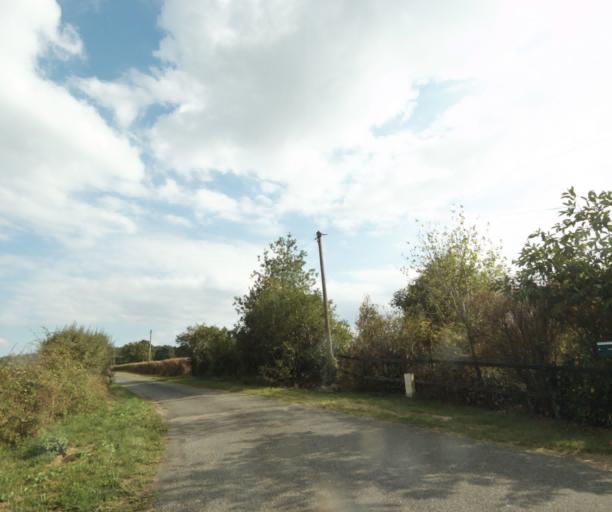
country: FR
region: Bourgogne
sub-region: Departement de Saone-et-Loire
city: Palinges
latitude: 46.5108
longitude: 4.2462
